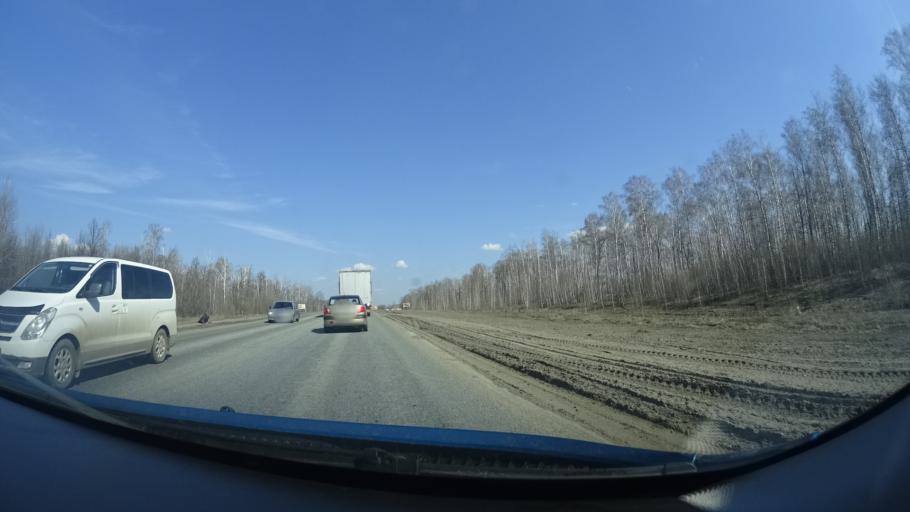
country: RU
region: Bashkortostan
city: Kandry
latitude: 54.5850
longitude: 54.2577
